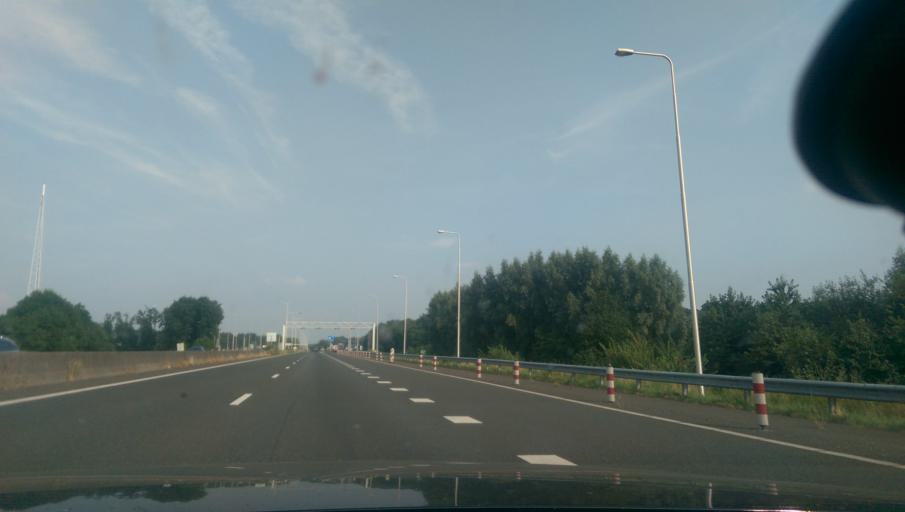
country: NL
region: Limburg
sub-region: Gemeente Venlo
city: Venlo
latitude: 51.3868
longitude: 6.2072
